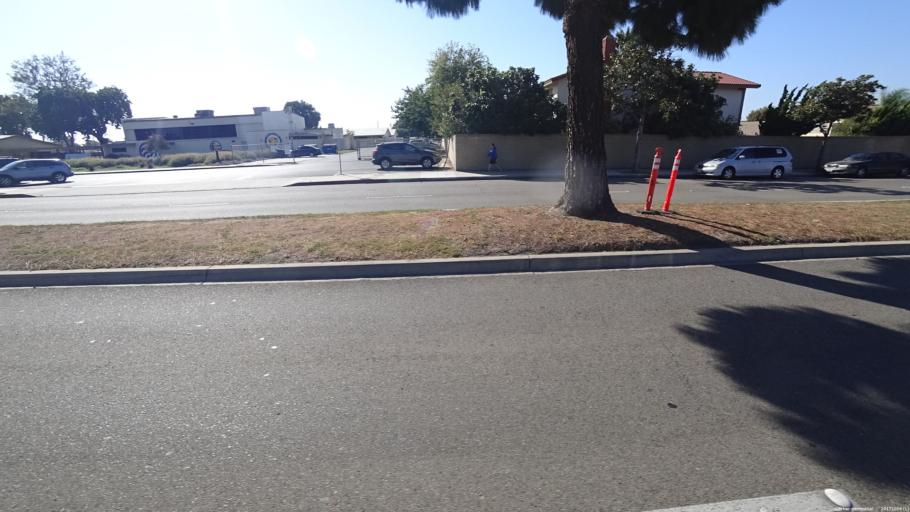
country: US
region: California
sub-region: Orange County
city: Stanton
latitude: 33.7785
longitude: -117.9753
